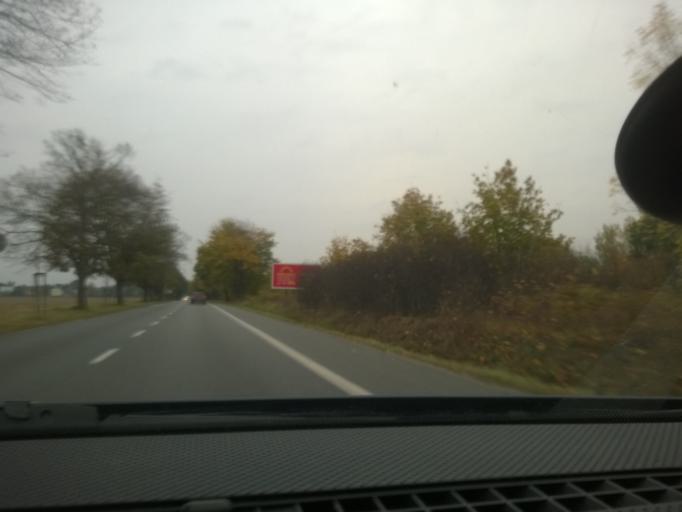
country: PL
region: Masovian Voivodeship
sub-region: Powiat pruszkowski
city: Komorow
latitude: 52.1569
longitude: 20.8332
